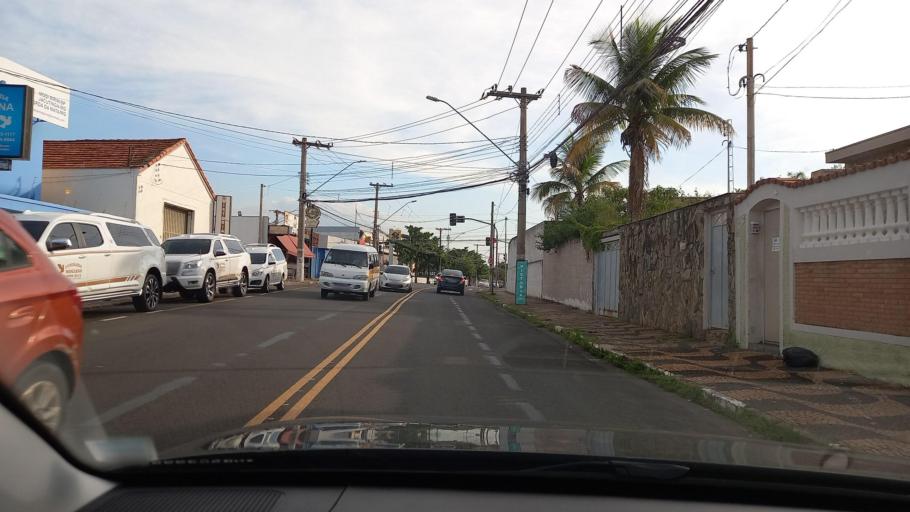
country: BR
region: Sao Paulo
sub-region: Mogi-Mirim
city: Mogi Mirim
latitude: -22.4402
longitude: -46.9660
